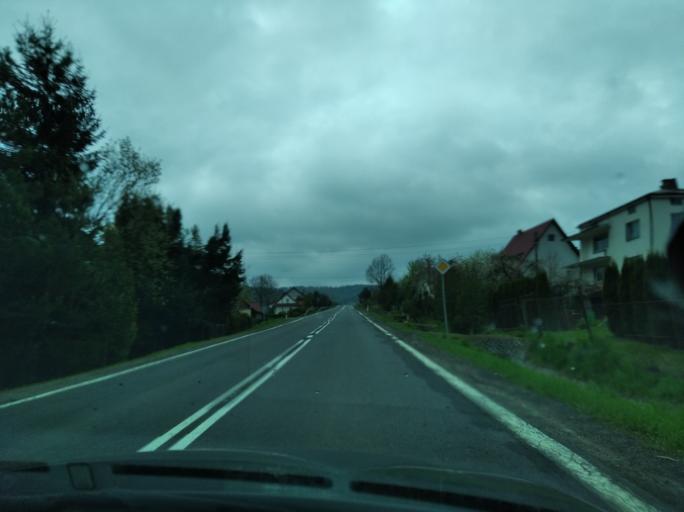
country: PL
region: Subcarpathian Voivodeship
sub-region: Powiat sanocki
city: Tyrawa Woloska
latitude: 49.5750
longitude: 22.3624
